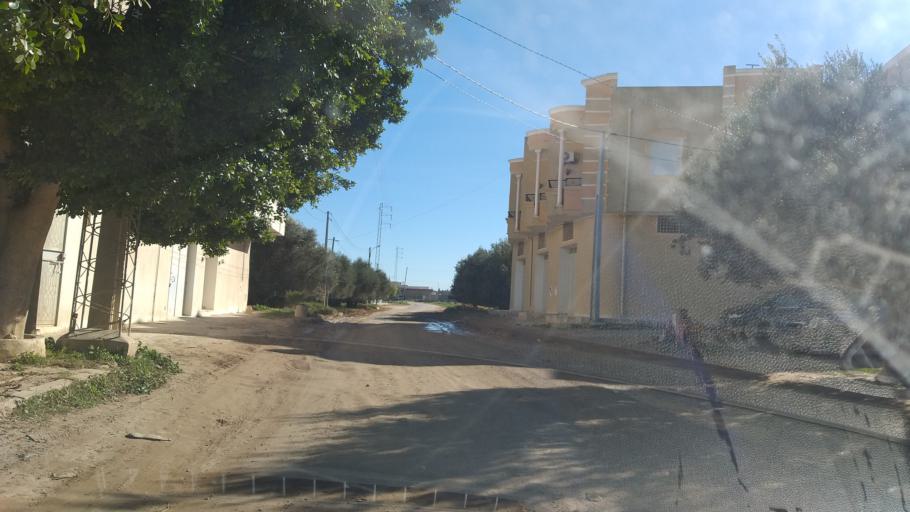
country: TN
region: Al Mahdiyah
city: El Jem
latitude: 35.2929
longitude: 10.7171
